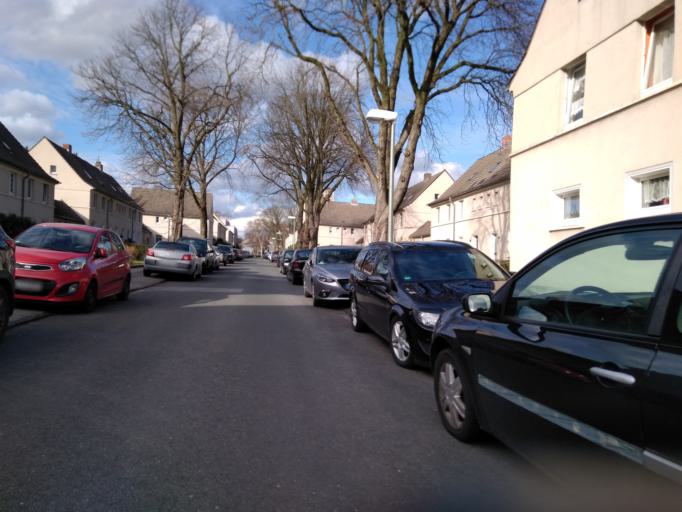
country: DE
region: North Rhine-Westphalia
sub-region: Regierungsbezirk Munster
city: Gladbeck
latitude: 51.5932
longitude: 7.0501
